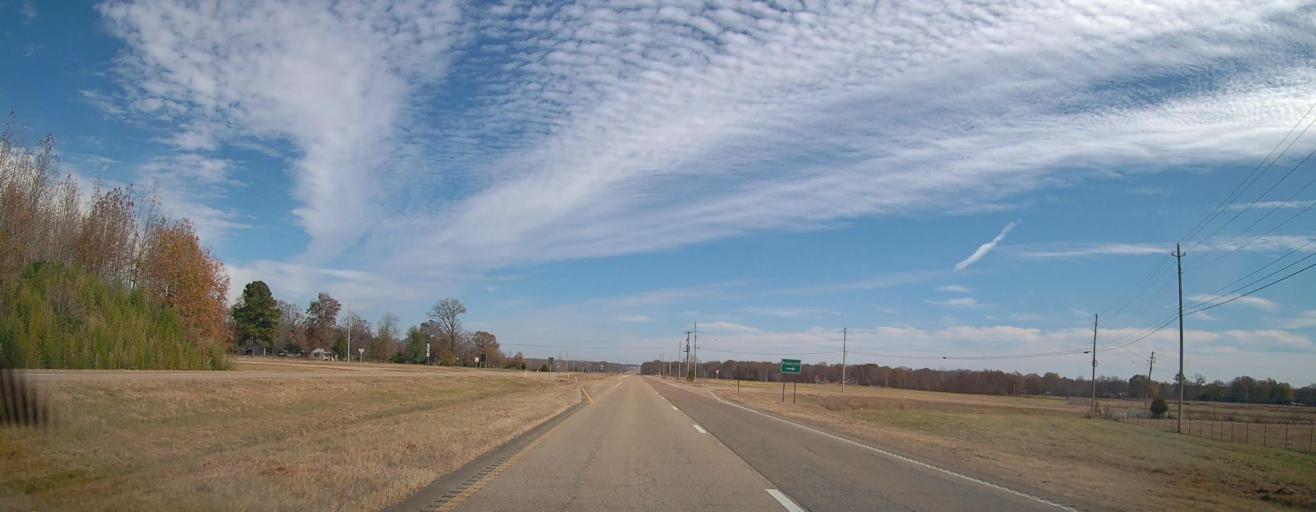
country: US
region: Mississippi
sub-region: Alcorn County
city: Corinth
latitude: 34.9310
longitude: -88.6308
